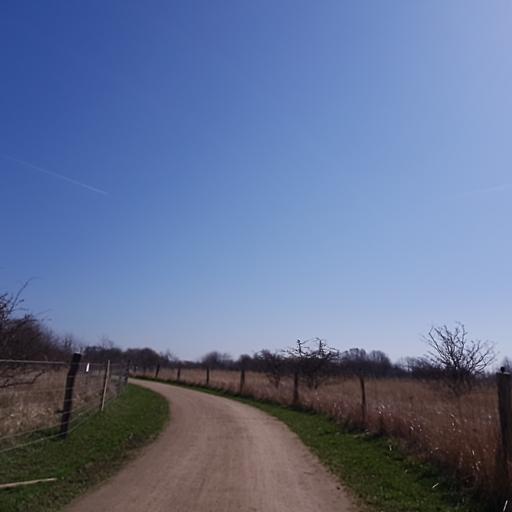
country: DK
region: Capital Region
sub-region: Frederiksberg Kommune
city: Frederiksberg
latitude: 55.6369
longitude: 12.5336
